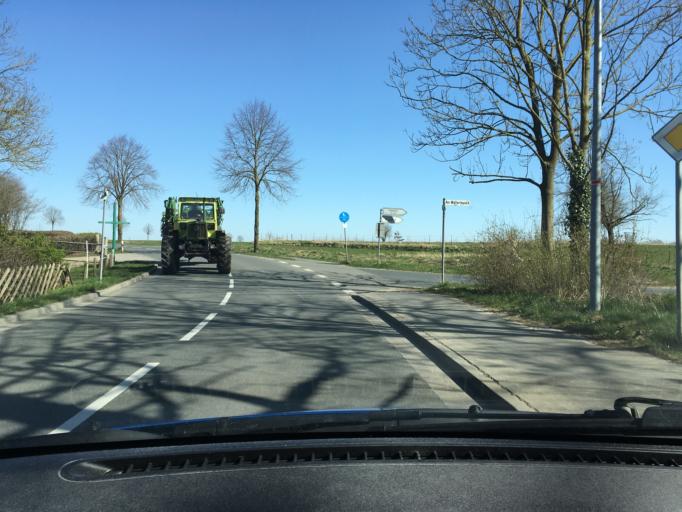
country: DE
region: Lower Saxony
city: Barum
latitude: 53.0027
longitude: 10.5132
